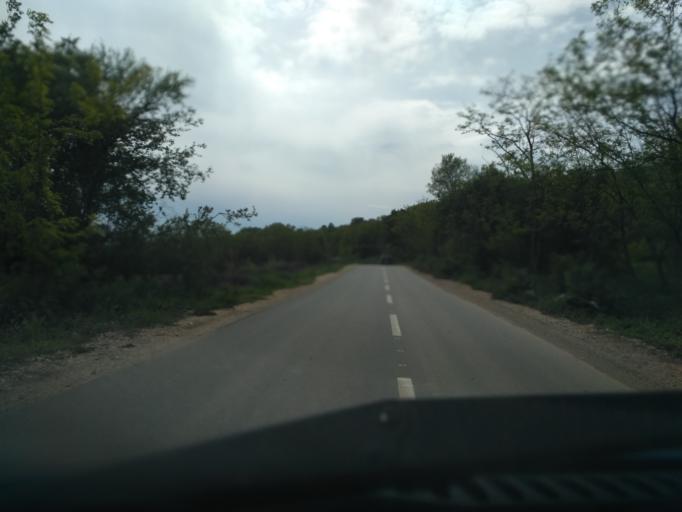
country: RS
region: Central Serbia
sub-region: Podunavski Okrug
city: Smederevska Palanka
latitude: 44.3623
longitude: 20.9881
